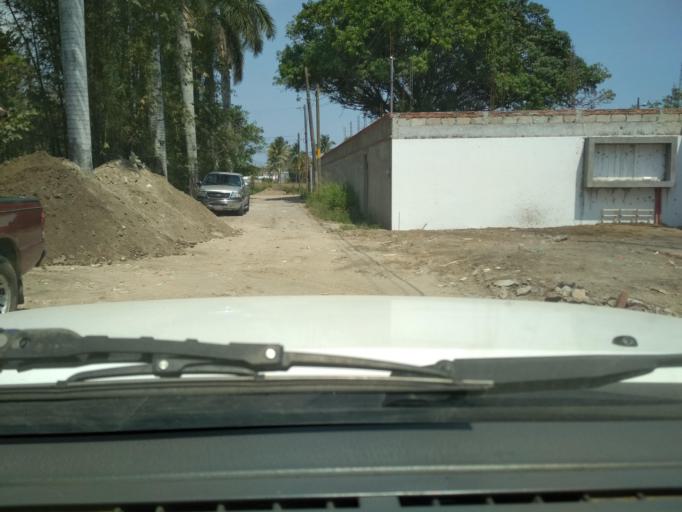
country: MX
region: Veracruz
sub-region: Medellin
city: Fraccionamiento Arboledas San Ramon
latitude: 19.0884
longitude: -96.1423
